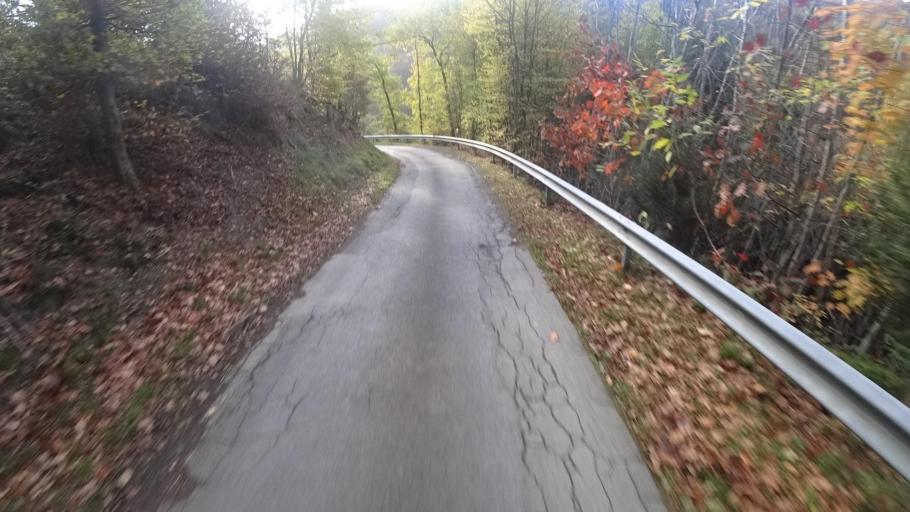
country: DE
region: Rheinland-Pfalz
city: Kirchsahr
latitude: 50.5119
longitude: 6.9127
